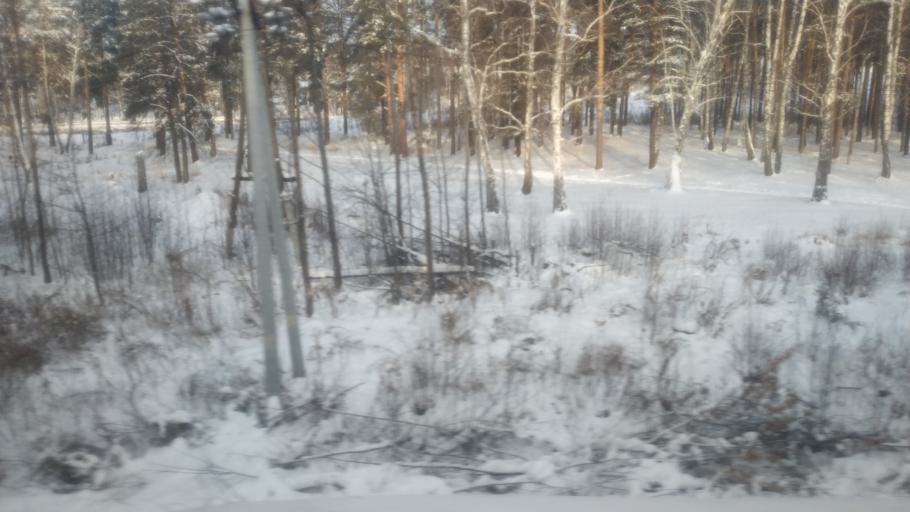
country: RU
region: Kirov
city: Krasnaya Polyana
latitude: 56.2511
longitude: 51.1467
